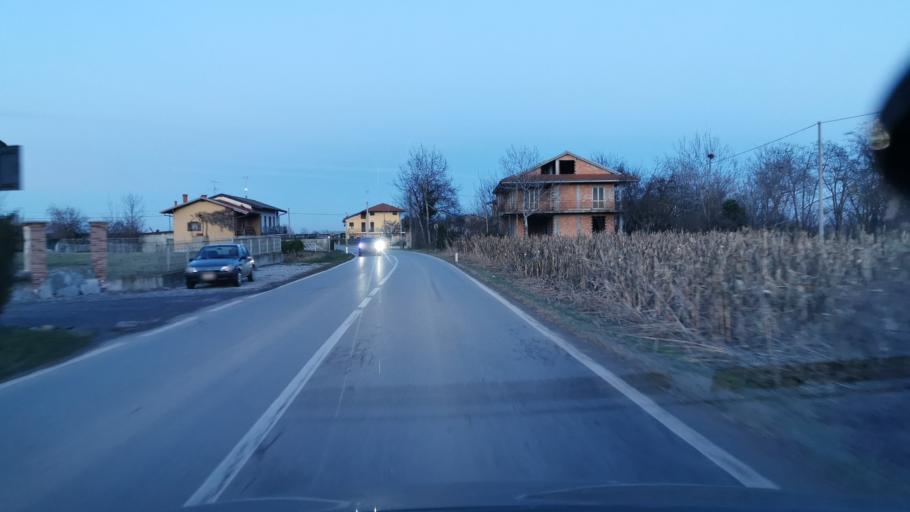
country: IT
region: Piedmont
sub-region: Provincia di Cuneo
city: Caraglio
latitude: 44.4348
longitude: 7.4563
